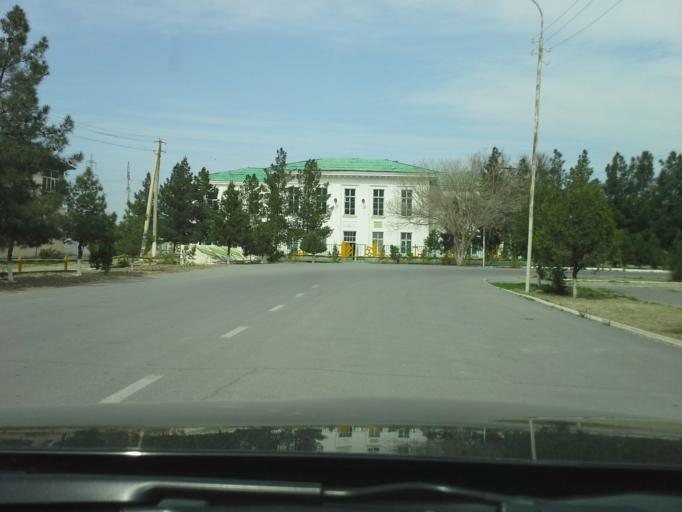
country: TM
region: Ahal
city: Abadan
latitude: 38.0621
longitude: 58.1550
